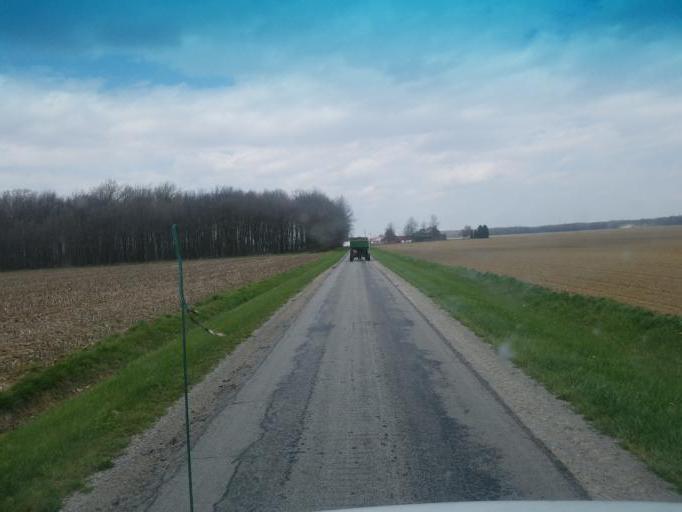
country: US
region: Ohio
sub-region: Crawford County
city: Bucyrus
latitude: 40.9695
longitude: -82.9972
